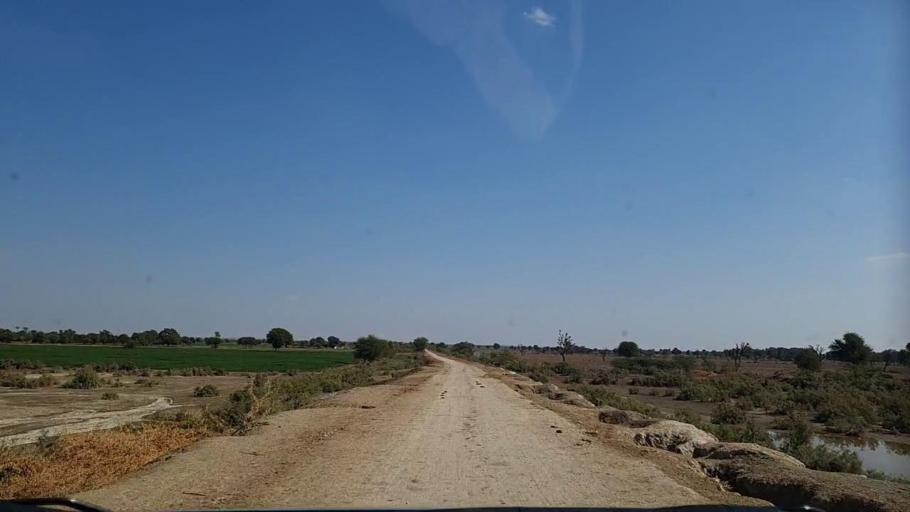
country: PK
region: Sindh
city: Pithoro
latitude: 25.6865
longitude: 69.4487
